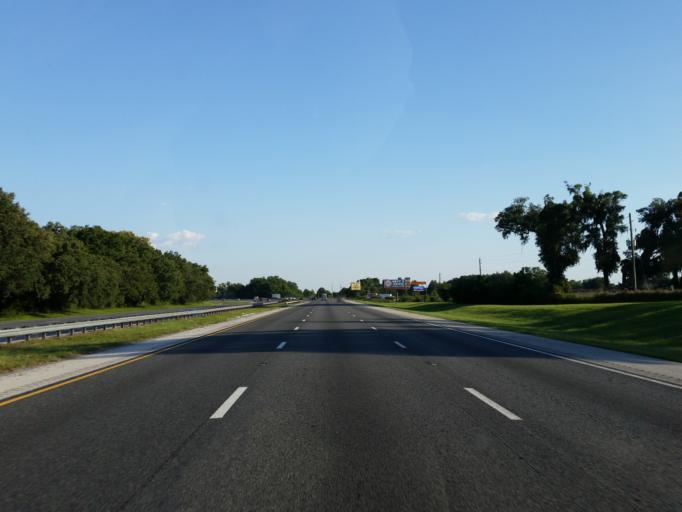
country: US
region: Florida
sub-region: Marion County
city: Ocala
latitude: 29.2392
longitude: -82.1901
